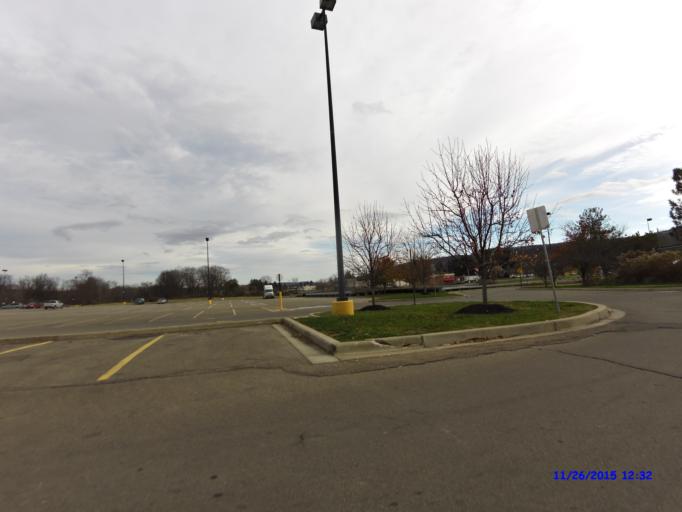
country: US
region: New York
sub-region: Cattaraugus County
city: Saint Bonaventure
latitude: 42.0783
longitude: -78.4688
